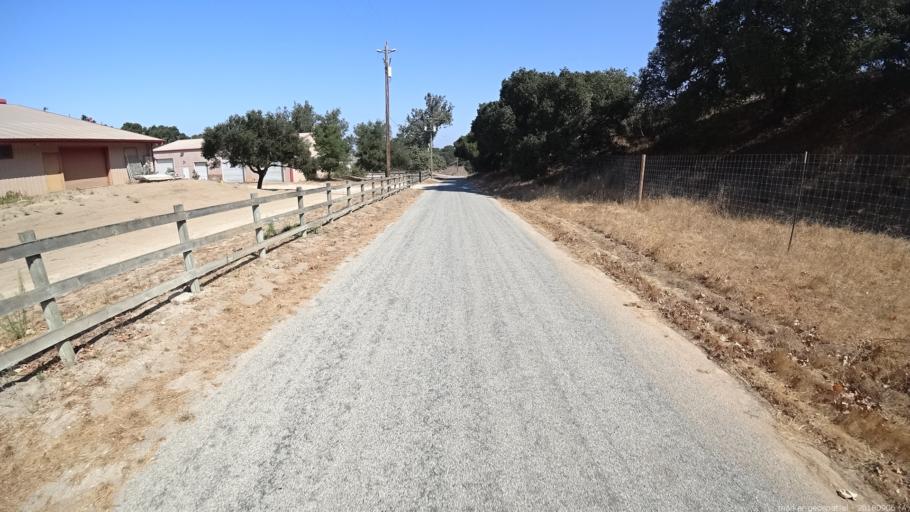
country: US
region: California
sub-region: Monterey County
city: Chualar
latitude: 36.5808
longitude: -121.6069
